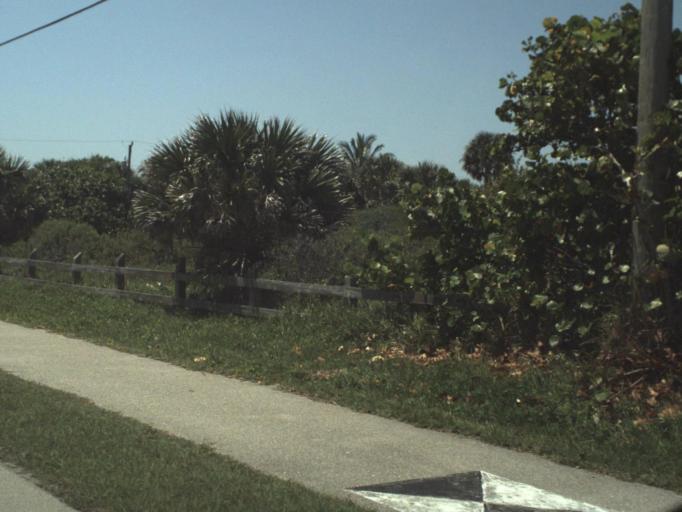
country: US
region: Florida
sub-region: Brevard County
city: Malabar
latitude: 27.9760
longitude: -80.5128
